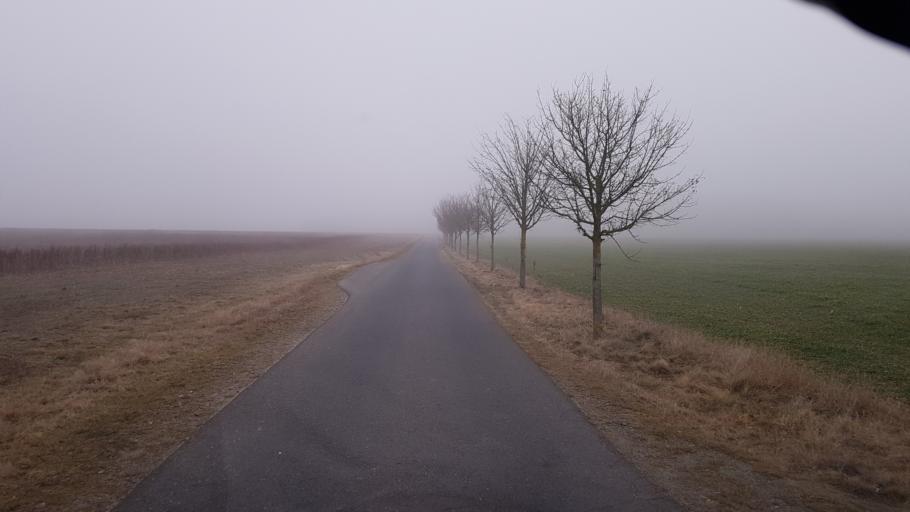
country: DE
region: Brandenburg
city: Ihlow
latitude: 51.8669
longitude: 13.2239
